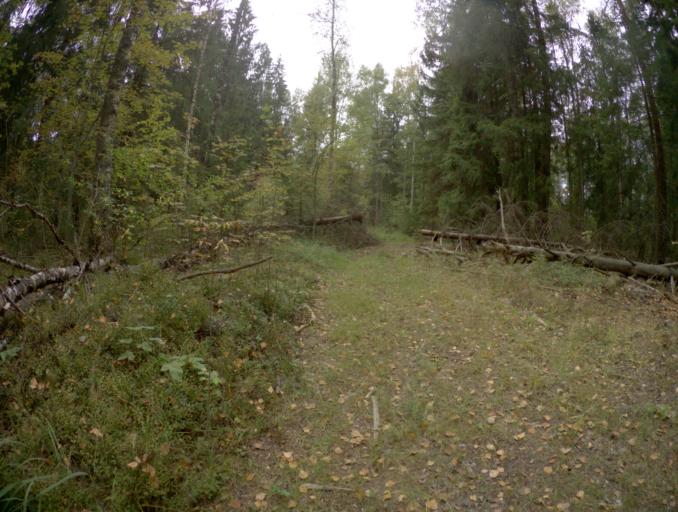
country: RU
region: Vladimir
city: Urshel'skiy
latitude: 55.8239
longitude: 40.2774
